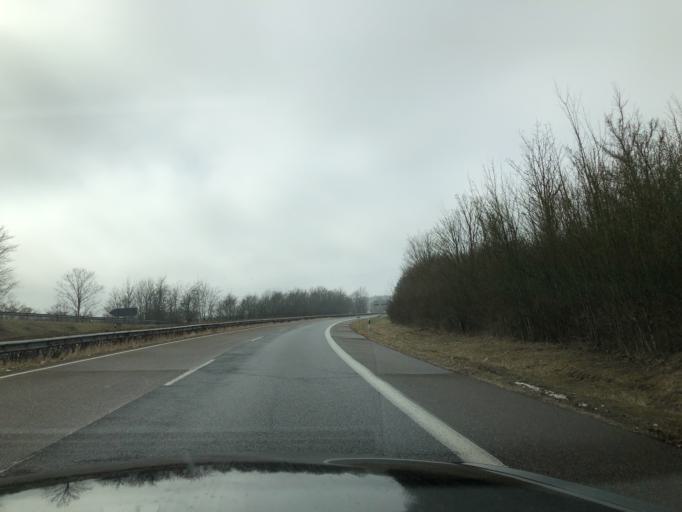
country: DE
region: Rheinland-Pfalz
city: Konigsfeld
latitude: 50.5339
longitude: 7.1942
